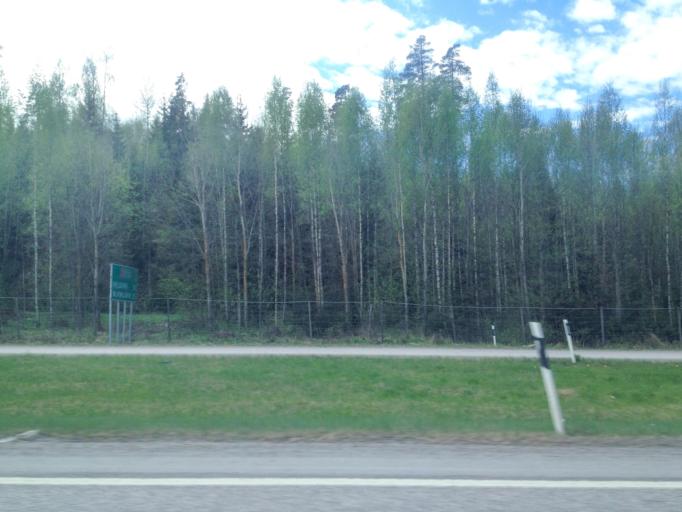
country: FI
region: Uusimaa
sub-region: Helsinki
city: Hyvinge
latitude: 60.6573
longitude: 24.7971
